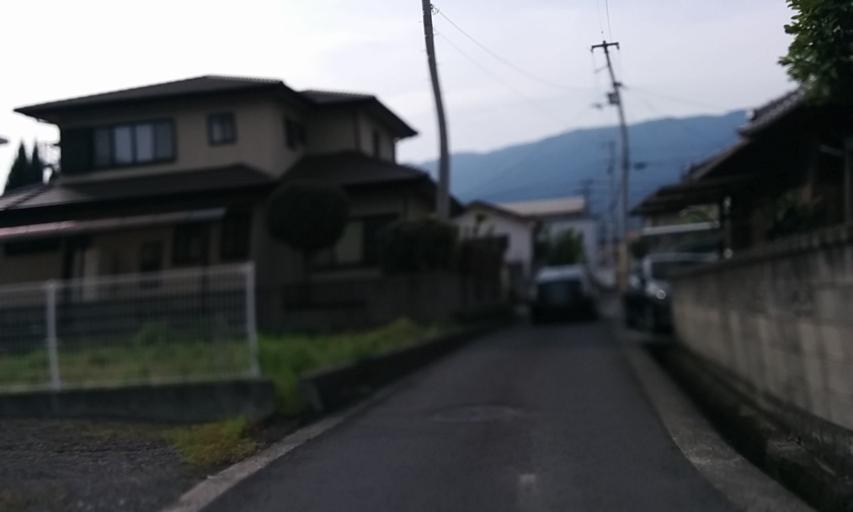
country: JP
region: Ehime
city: Kawanoecho
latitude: 33.9839
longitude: 133.5541
